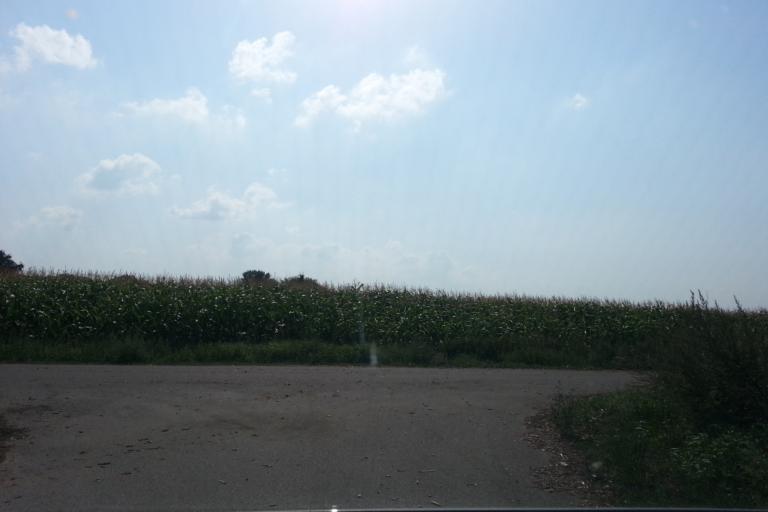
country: DE
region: Mecklenburg-Vorpommern
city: Ferdinandshof
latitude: 53.6266
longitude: 13.7980
